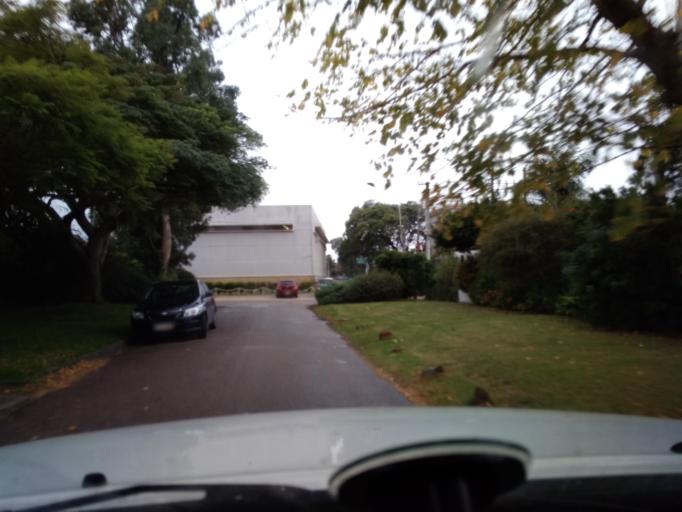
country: UY
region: Canelones
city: Barra de Carrasco
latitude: -34.8823
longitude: -56.0424
